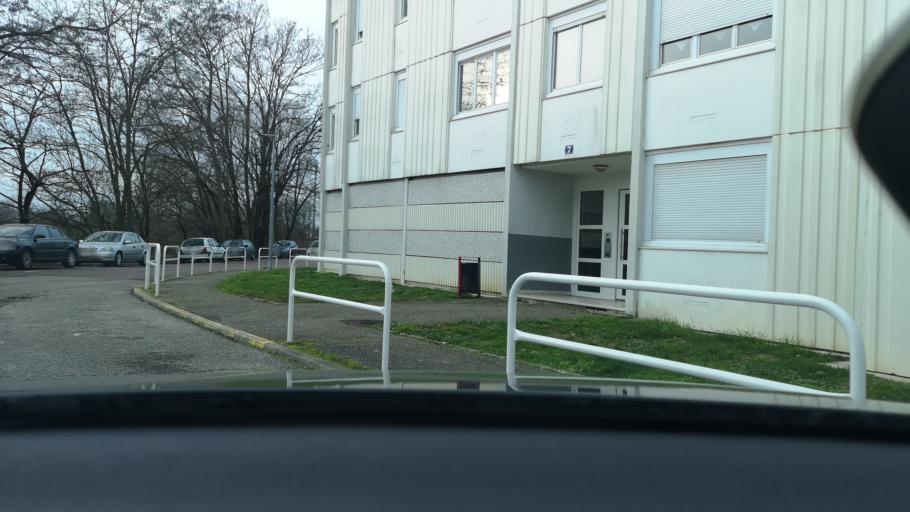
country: FR
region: Bourgogne
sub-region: Departement de Saone-et-Loire
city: Chalon-sur-Saone
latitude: 46.7785
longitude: 4.8353
